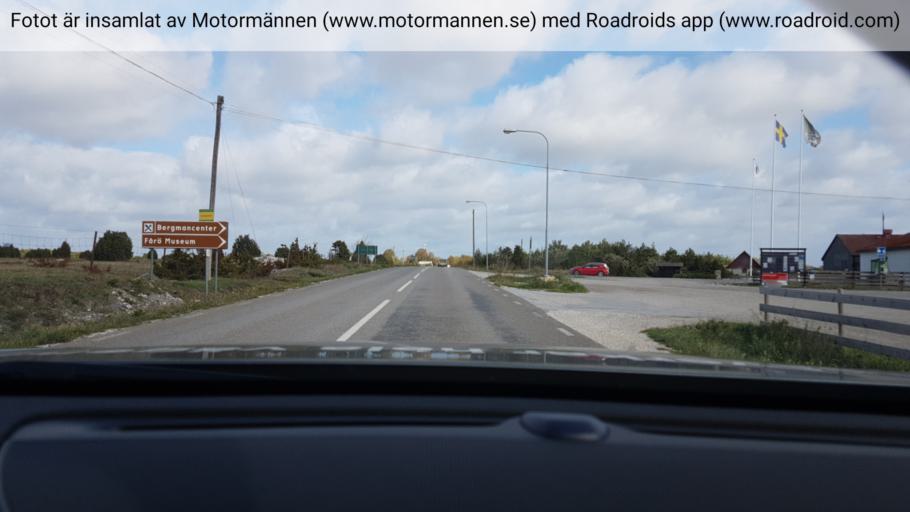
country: SE
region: Gotland
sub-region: Gotland
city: Slite
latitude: 57.9184
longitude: 19.1372
